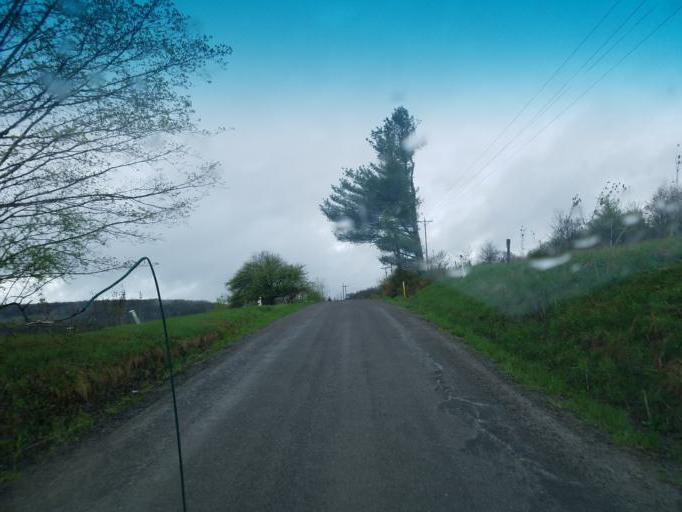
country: US
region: Pennsylvania
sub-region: Tioga County
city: Westfield
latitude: 41.9790
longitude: -77.6828
